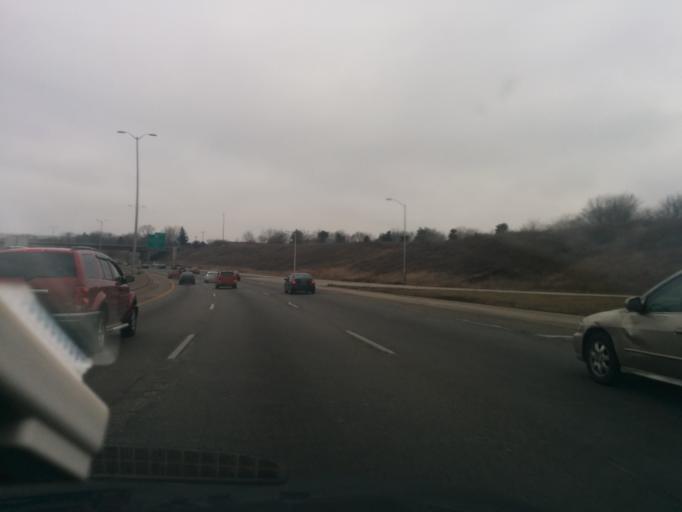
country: US
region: Wisconsin
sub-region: Milwaukee County
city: Milwaukee
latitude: 43.0587
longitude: -87.9233
